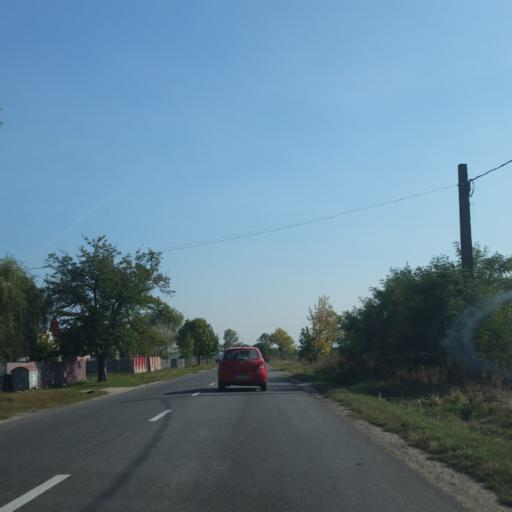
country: RO
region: Arges
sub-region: Comuna Merisani
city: Merisani
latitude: 45.0108
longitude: 24.7241
